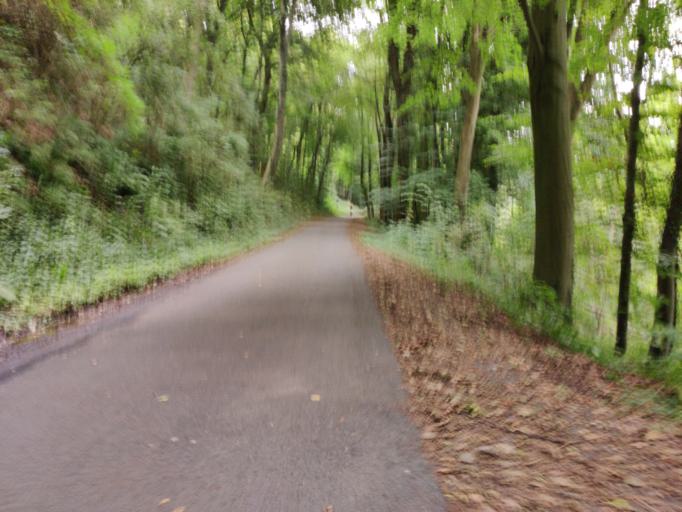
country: DE
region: Lower Saxony
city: Heyen
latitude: 51.9961
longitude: 9.5068
